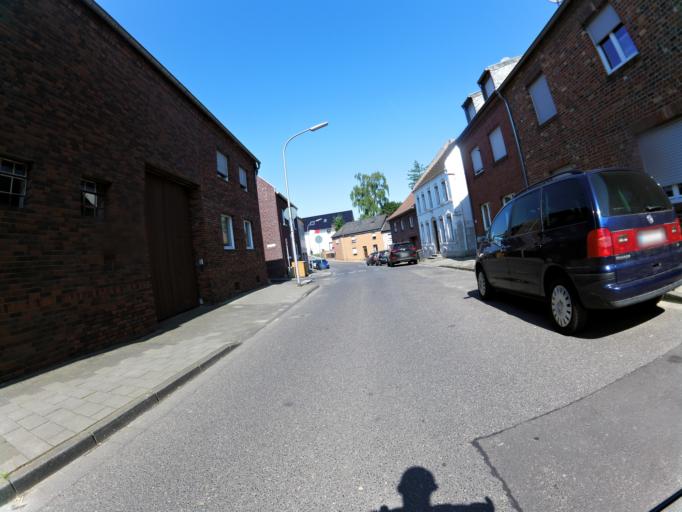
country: DE
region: North Rhine-Westphalia
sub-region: Regierungsbezirk Koln
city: Linnich
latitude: 51.0031
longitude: 6.2448
